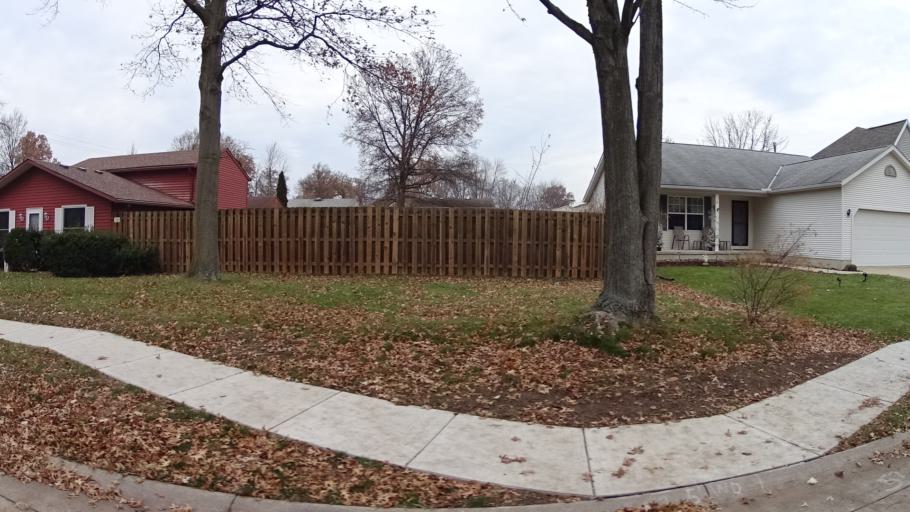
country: US
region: Ohio
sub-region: Lorain County
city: North Ridgeville
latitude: 41.4029
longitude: -82.0087
